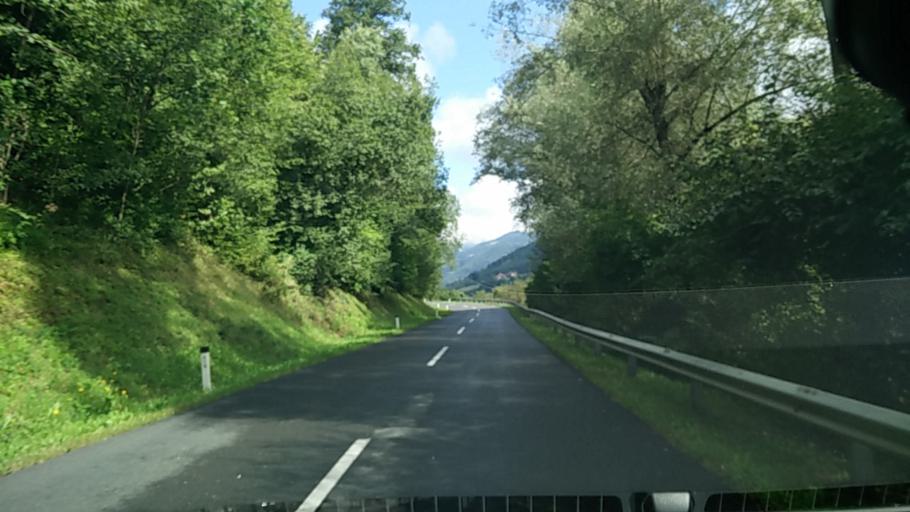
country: AT
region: Carinthia
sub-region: Politischer Bezirk Volkermarkt
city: Voelkermarkt
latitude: 46.6676
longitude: 14.5748
